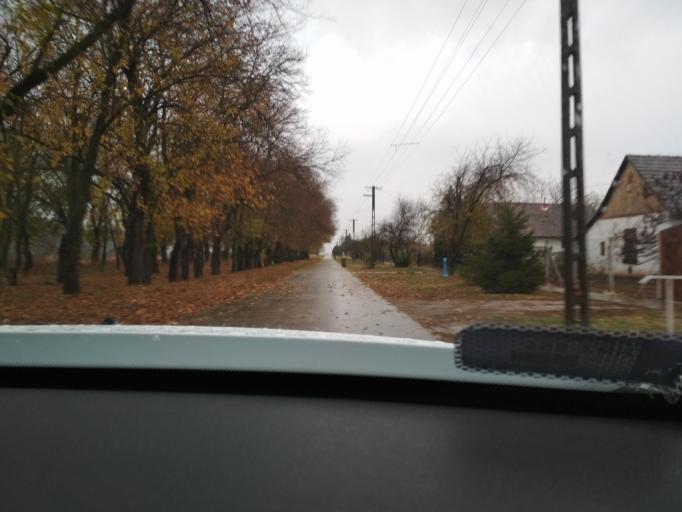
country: HU
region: Csongrad
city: Opusztaszer
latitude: 46.4352
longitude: 20.1412
